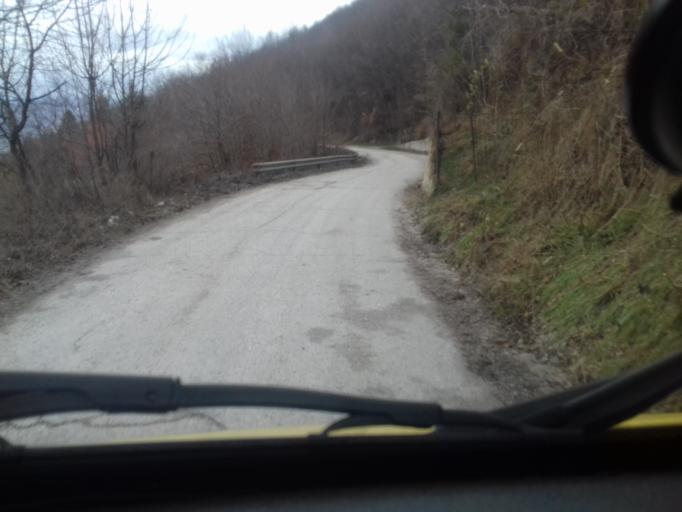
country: BA
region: Federation of Bosnia and Herzegovina
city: Zenica
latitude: 44.2271
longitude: 17.9546
